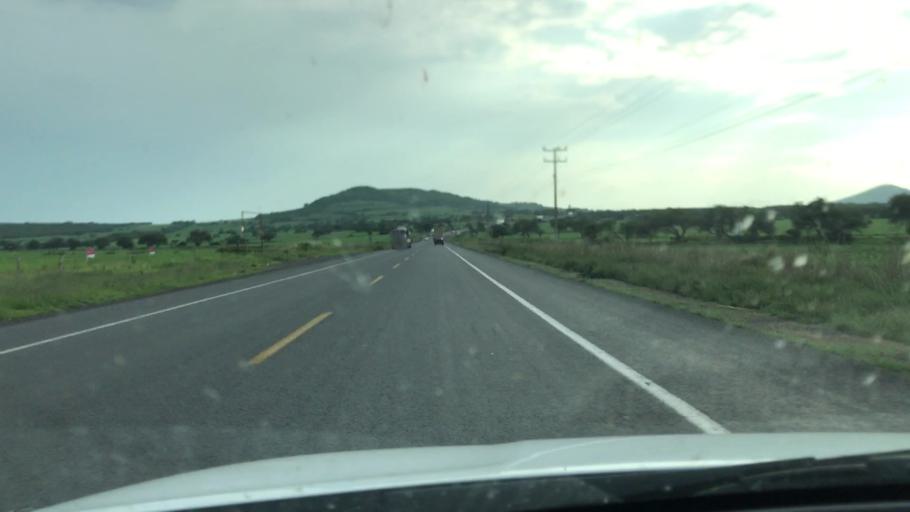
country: MX
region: Michoacan
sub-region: Yurecuaro
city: Yurecuaro
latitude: 20.3388
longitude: -102.1836
